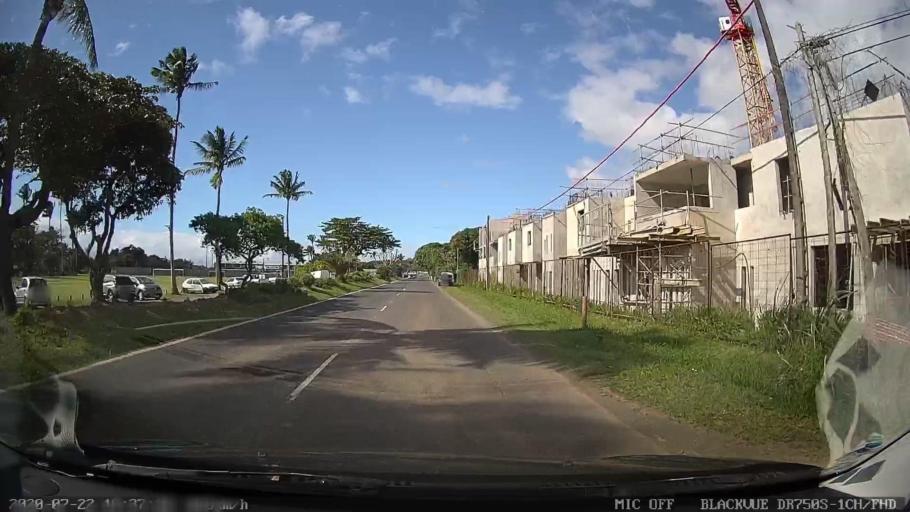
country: RE
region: Reunion
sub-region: Reunion
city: Sainte-Suzanne
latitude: -20.9110
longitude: 55.6116
